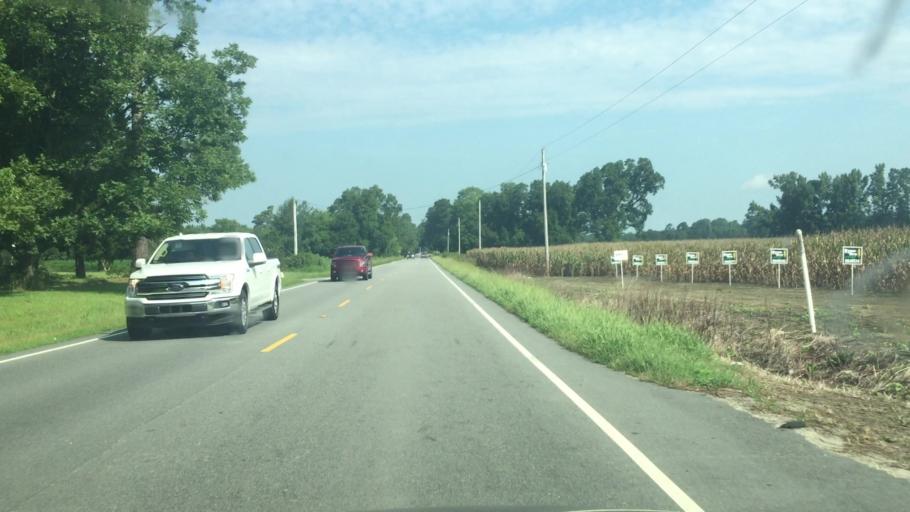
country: US
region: North Carolina
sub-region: Columbus County
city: Chadbourn
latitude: 34.2859
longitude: -78.8210
